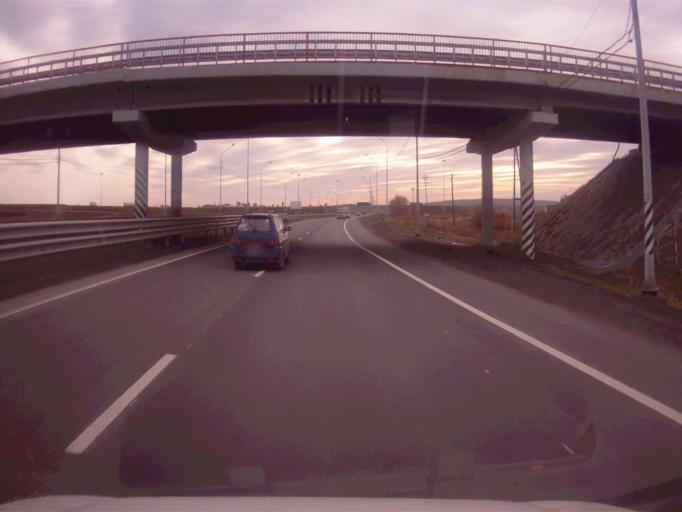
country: RU
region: Chelyabinsk
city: Novosineglazovskiy
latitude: 55.0021
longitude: 61.4539
